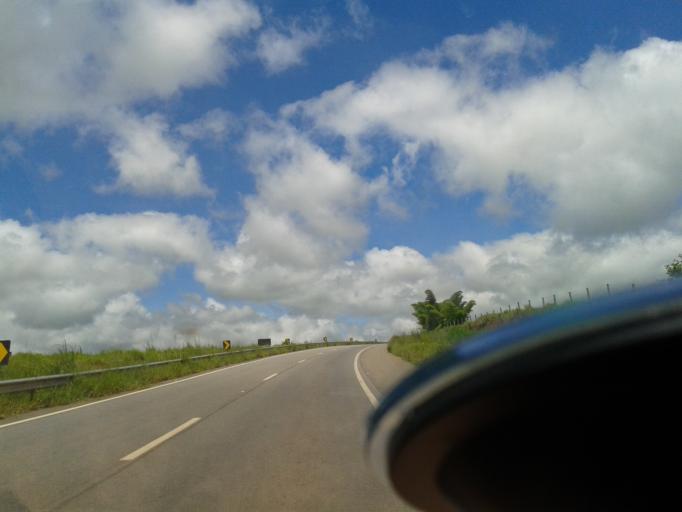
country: BR
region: Goias
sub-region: Itaberai
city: Itaberai
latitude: -16.0963
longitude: -49.7083
